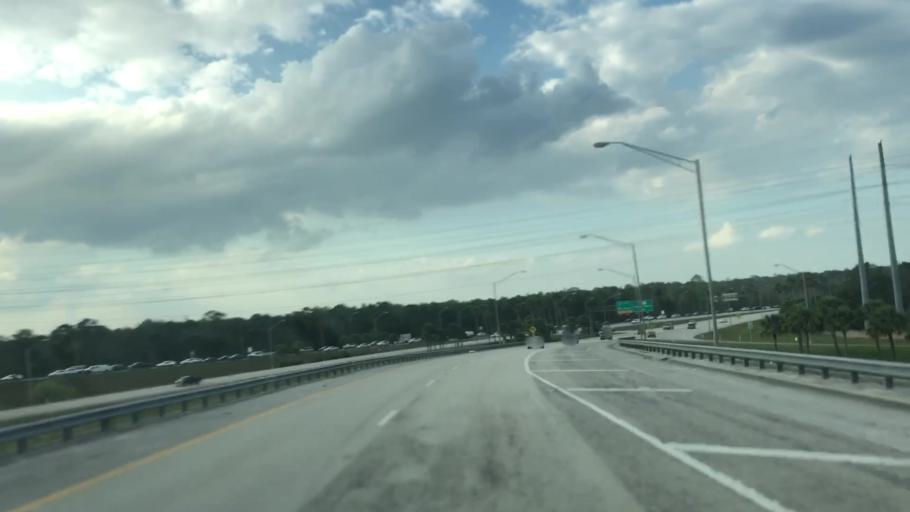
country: US
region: Florida
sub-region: Osceola County
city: Celebration
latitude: 28.3077
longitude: -81.5708
